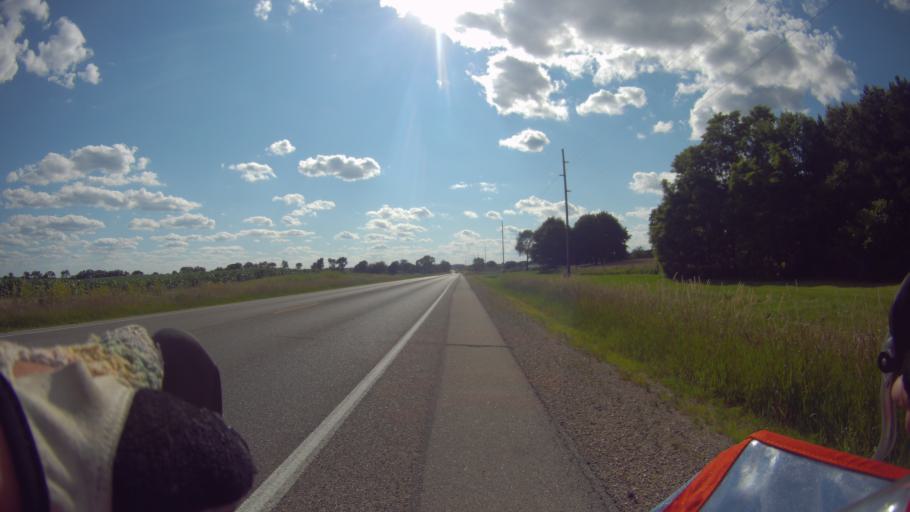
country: US
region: Wisconsin
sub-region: Dane County
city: Stoughton
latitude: 42.9189
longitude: -89.2860
